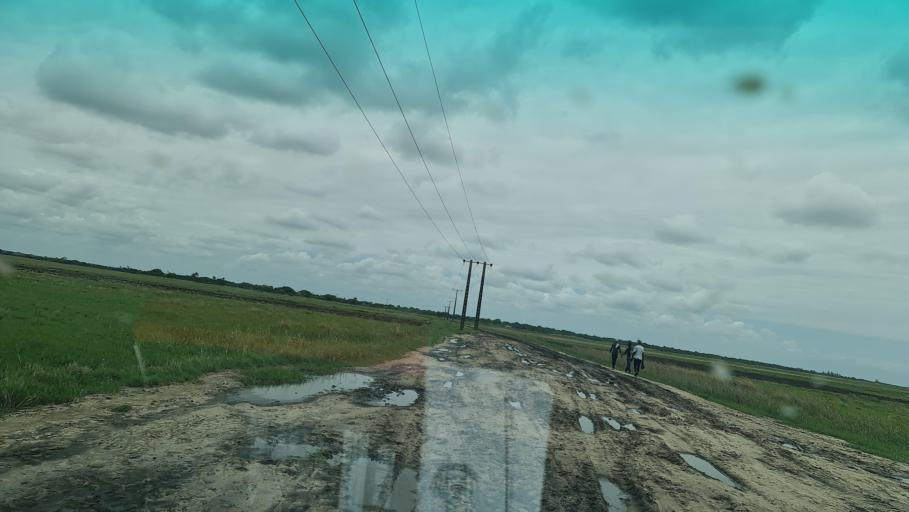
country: MZ
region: Maputo City
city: Maputo
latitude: -25.7113
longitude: 32.7029
